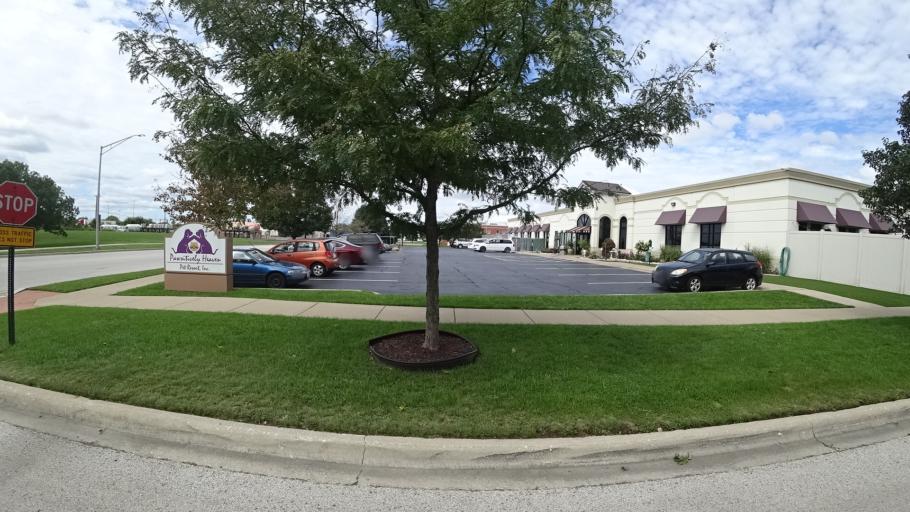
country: US
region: Illinois
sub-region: Cook County
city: Chicago Ridge
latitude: 41.7055
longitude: -87.7889
